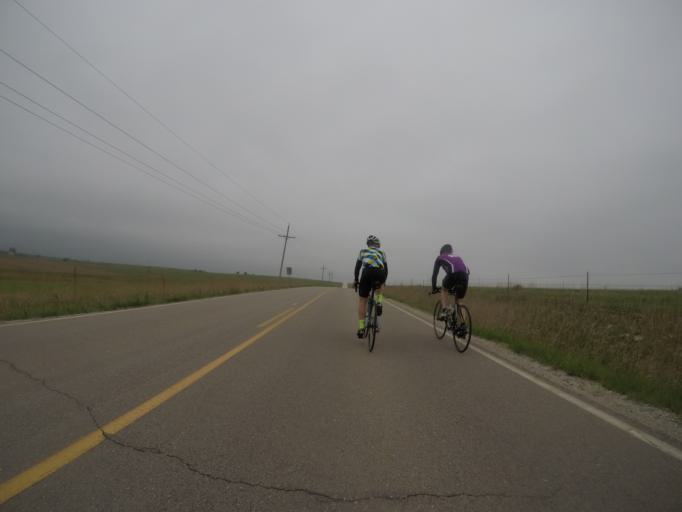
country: US
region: Kansas
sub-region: Pottawatomie County
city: Westmoreland
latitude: 39.5203
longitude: -96.3142
